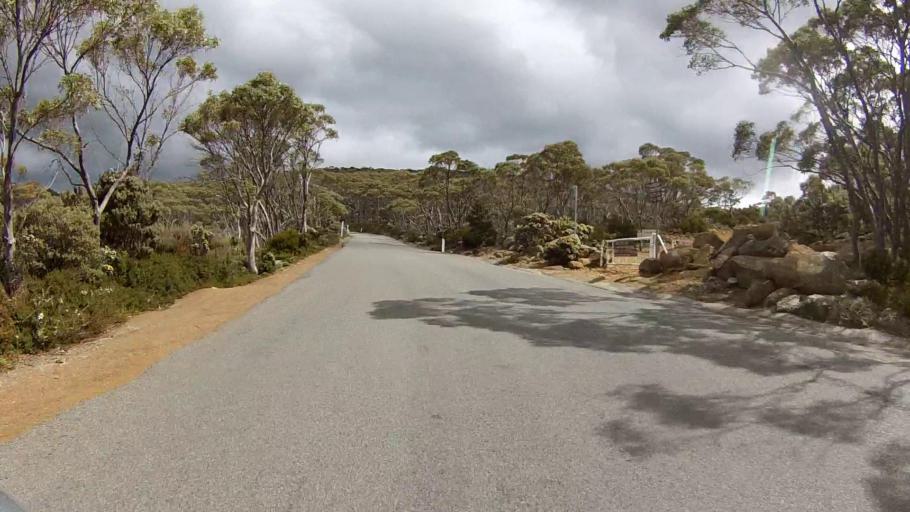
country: AU
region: Tasmania
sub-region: Glenorchy
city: West Moonah
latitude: -42.8853
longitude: 147.2213
